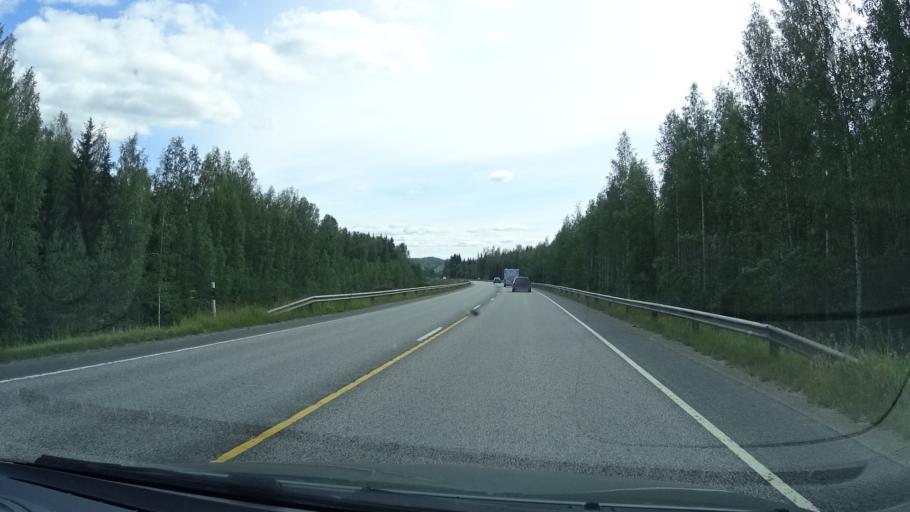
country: FI
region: Central Finland
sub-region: Jyvaeskylae
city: Jyvaeskylae
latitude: 62.2619
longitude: 25.5920
